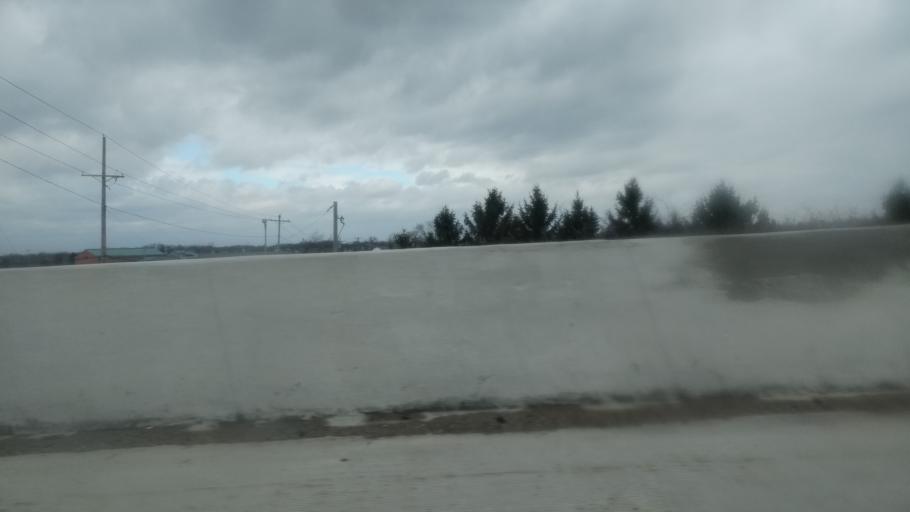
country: US
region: Ohio
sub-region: Lucas County
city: Maumee
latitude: 41.5329
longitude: -83.6553
